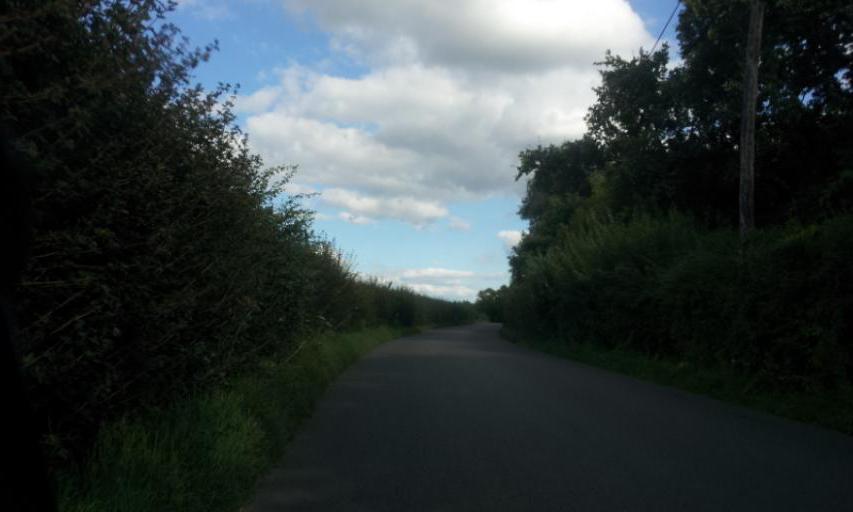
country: GB
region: England
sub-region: Kent
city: Headcorn
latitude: 51.1701
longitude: 0.6091
